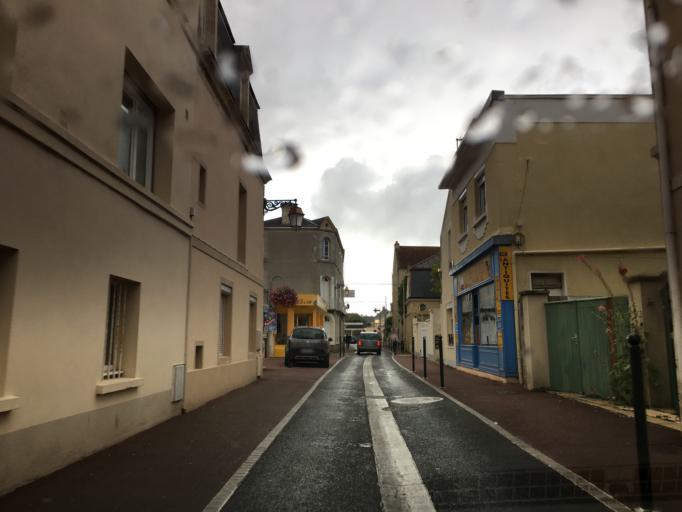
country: FR
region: Lower Normandy
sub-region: Departement du Calvados
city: Saint-Aubin-sur-Mer
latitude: 49.3307
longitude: -0.3902
